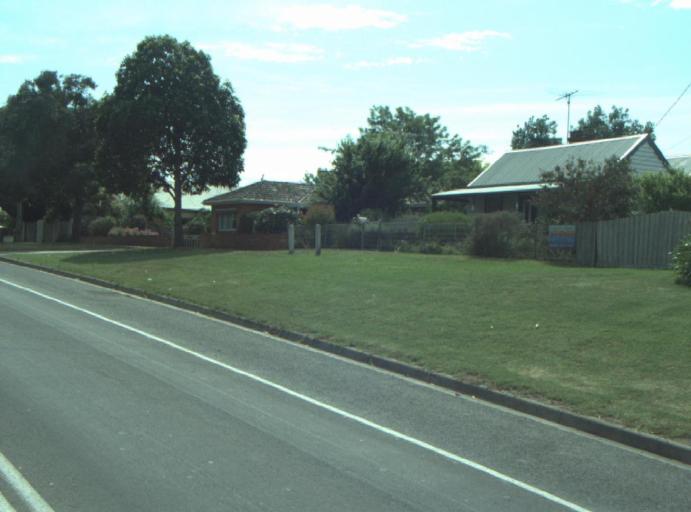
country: AU
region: Victoria
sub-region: Greater Geelong
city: Clifton Springs
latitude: -38.1774
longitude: 144.5651
